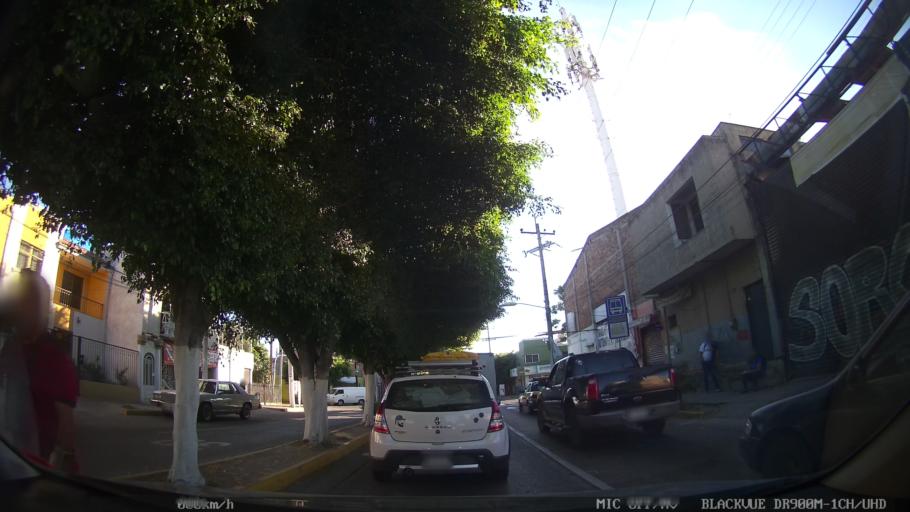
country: MX
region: Jalisco
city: Tlaquepaque
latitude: 20.6283
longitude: -103.3200
